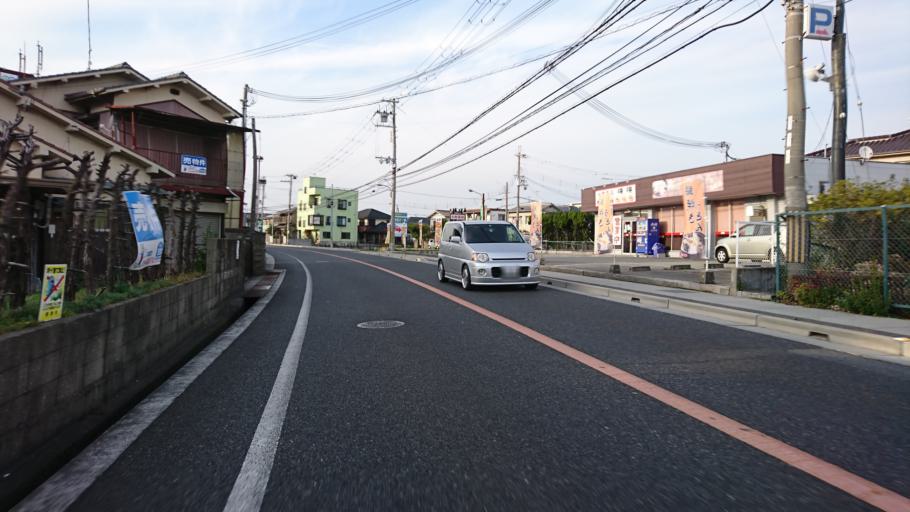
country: JP
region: Hyogo
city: Kakogawacho-honmachi
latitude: 34.7163
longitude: 134.8606
